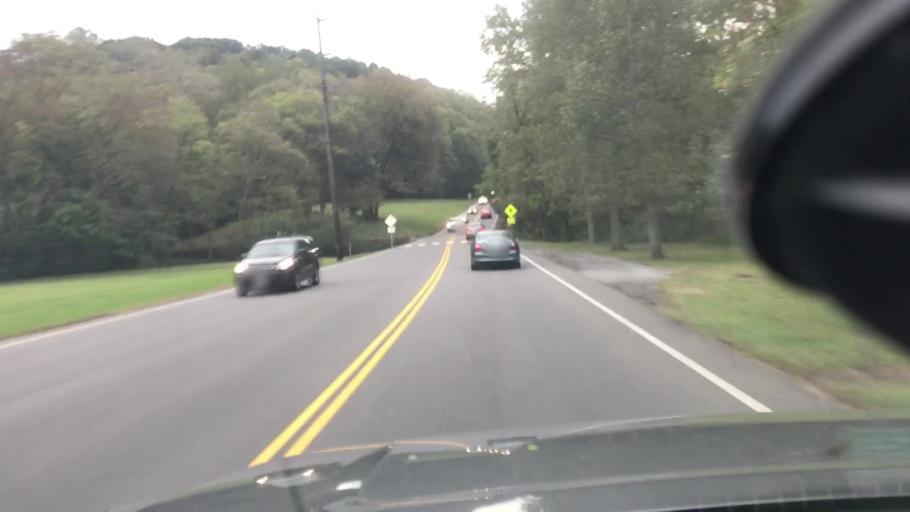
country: US
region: Tennessee
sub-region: Davidson County
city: Belle Meade
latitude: 36.0611
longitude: -86.9040
